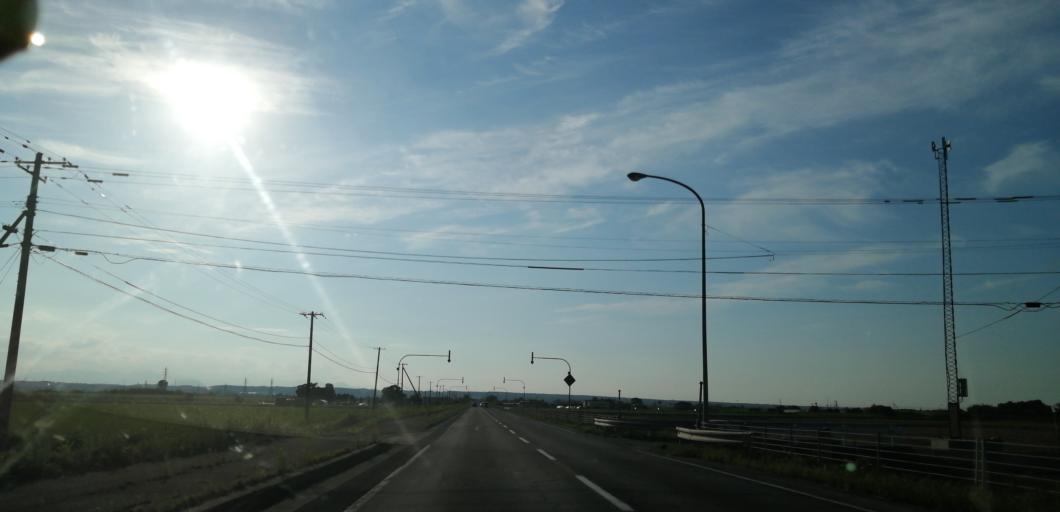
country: JP
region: Hokkaido
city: Kitahiroshima
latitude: 42.9915
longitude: 141.6038
